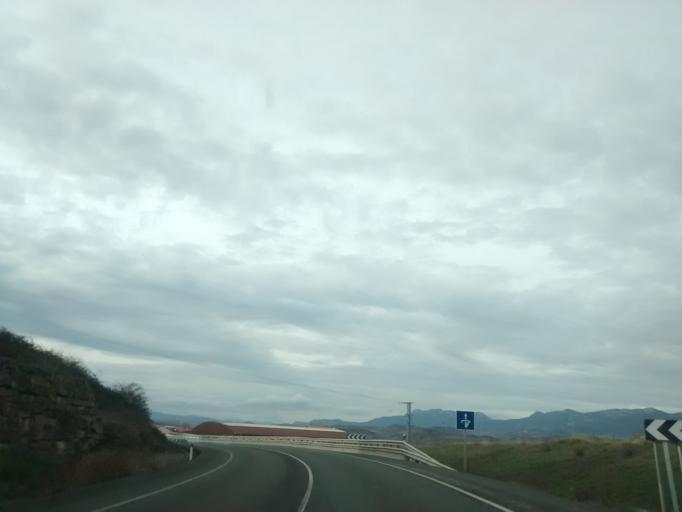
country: ES
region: La Rioja
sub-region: Provincia de La Rioja
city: Cenicero
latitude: 42.4796
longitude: -2.6441
